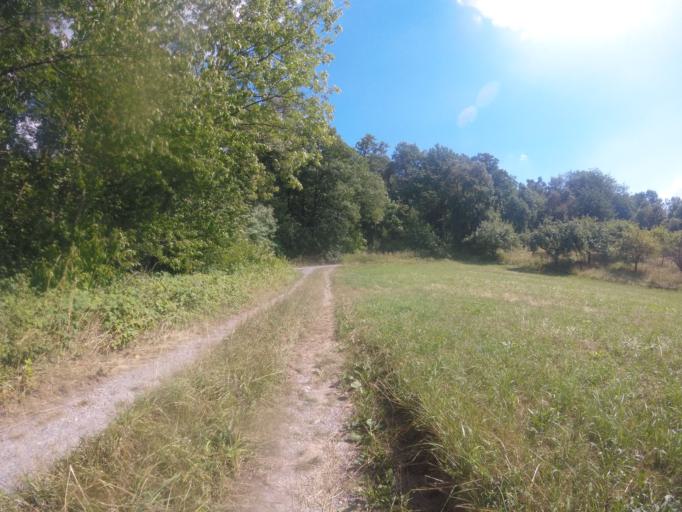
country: DE
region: Baden-Wuerttemberg
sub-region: Regierungsbezirk Stuttgart
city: Abstatt
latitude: 49.0720
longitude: 9.3187
